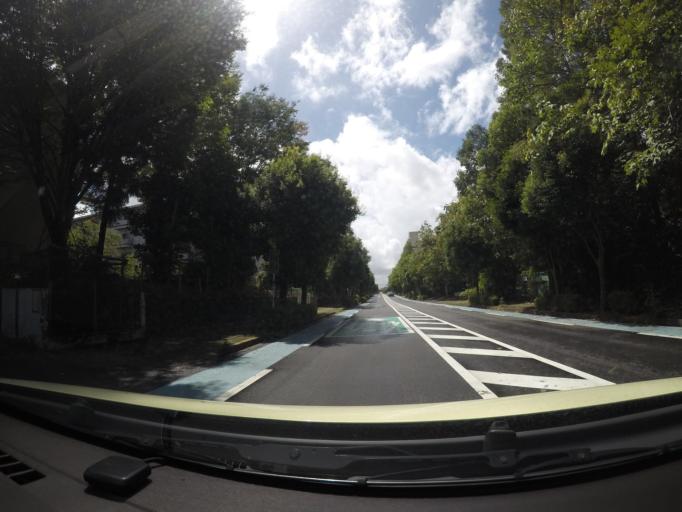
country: JP
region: Ibaraki
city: Naka
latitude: 36.0867
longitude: 140.1136
